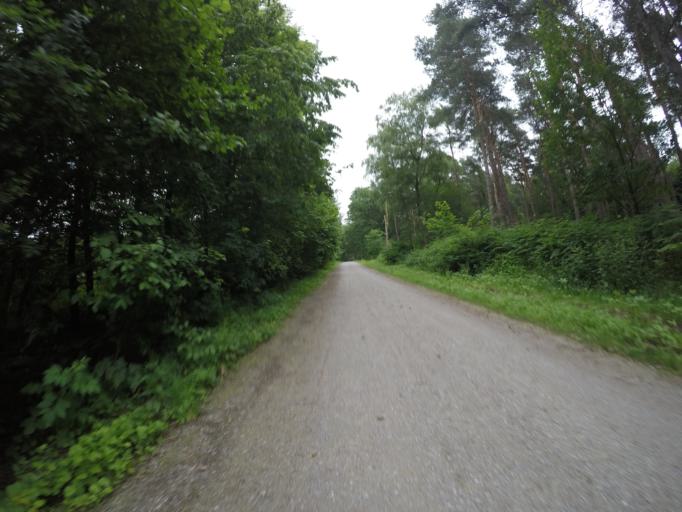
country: DE
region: North Rhine-Westphalia
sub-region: Regierungsbezirk Dusseldorf
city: Schermbeck
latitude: 51.5940
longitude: 6.8636
